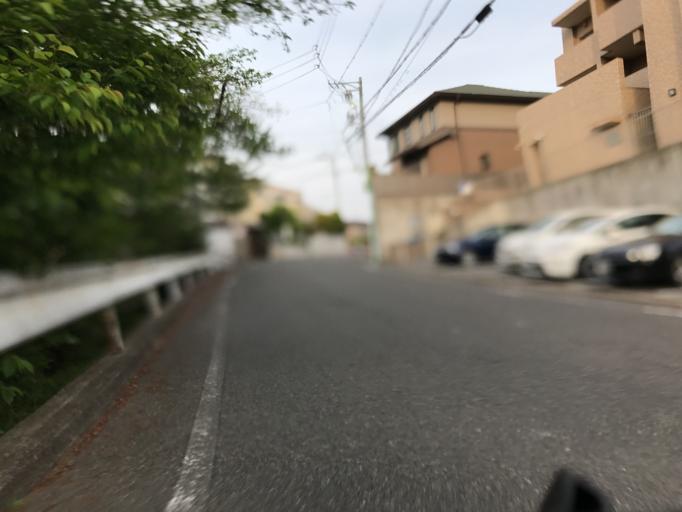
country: JP
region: Aichi
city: Nagoya-shi
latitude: 35.1699
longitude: 136.9521
